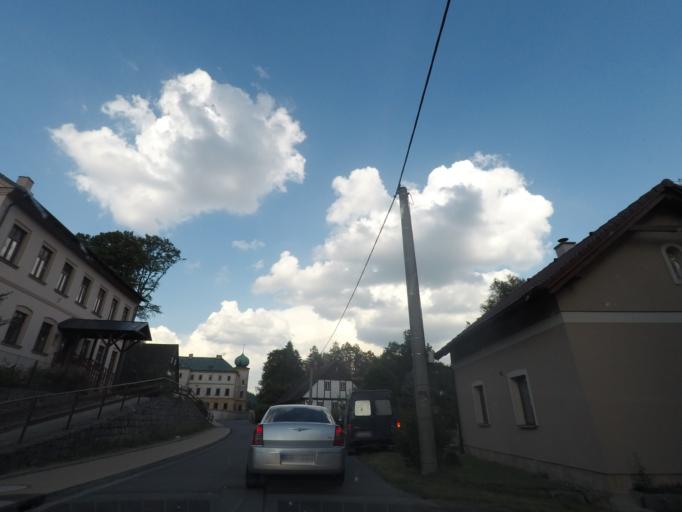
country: CZ
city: Teplice nad Metuji
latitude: 50.6186
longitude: 16.1089
